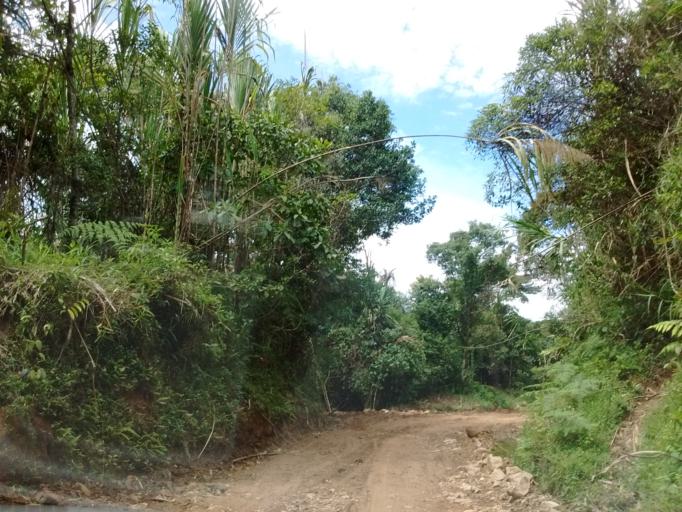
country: CO
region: Cauca
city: Morales
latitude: 2.6836
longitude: -76.7612
